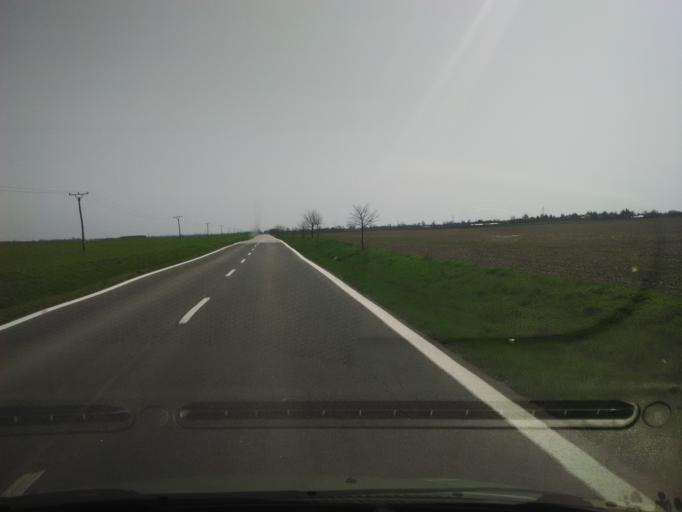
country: SK
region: Nitriansky
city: Surany
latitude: 48.0499
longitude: 18.1136
